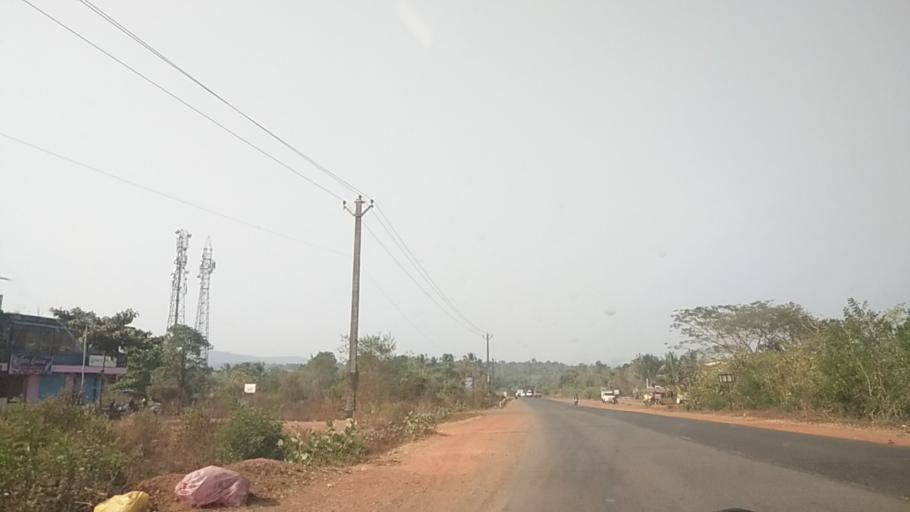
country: IN
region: Goa
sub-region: North Goa
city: Colovale
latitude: 15.6672
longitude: 73.8384
